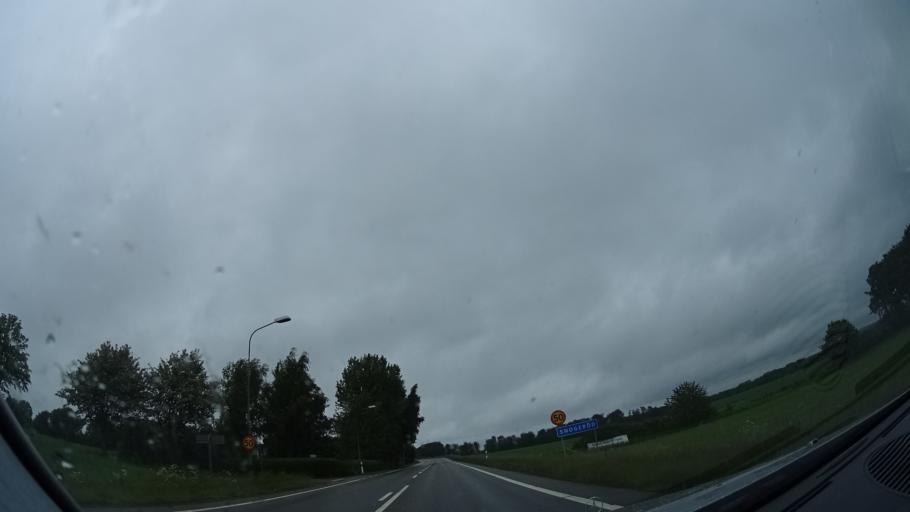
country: SE
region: Skane
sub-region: Hoors Kommun
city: Loberod
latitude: 55.8329
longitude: 13.4940
